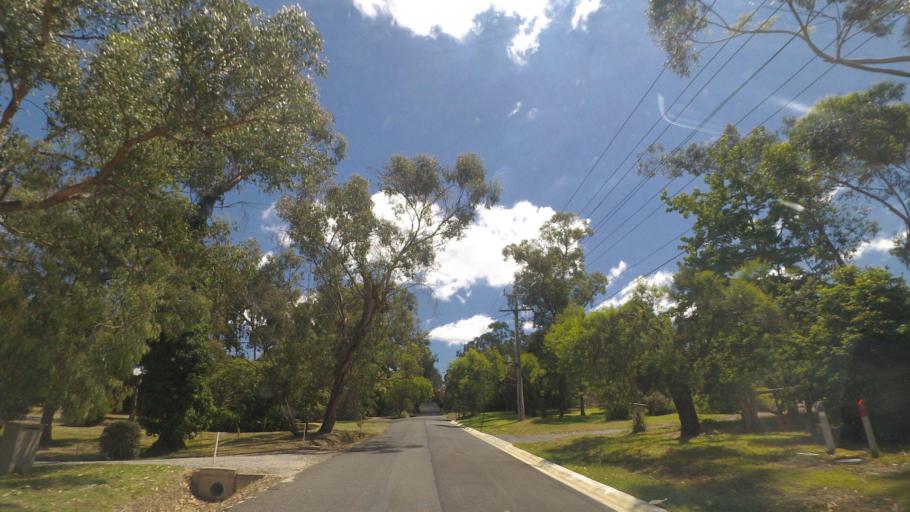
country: AU
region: Victoria
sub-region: Maroondah
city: Croydon Hills
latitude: -37.7388
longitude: 145.2746
